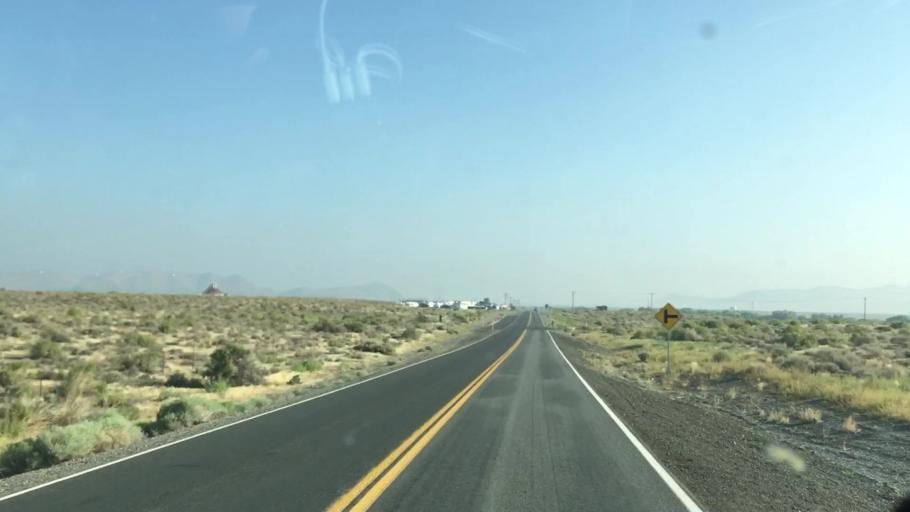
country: US
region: Nevada
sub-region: Lyon County
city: Fernley
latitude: 39.8149
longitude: -119.3636
